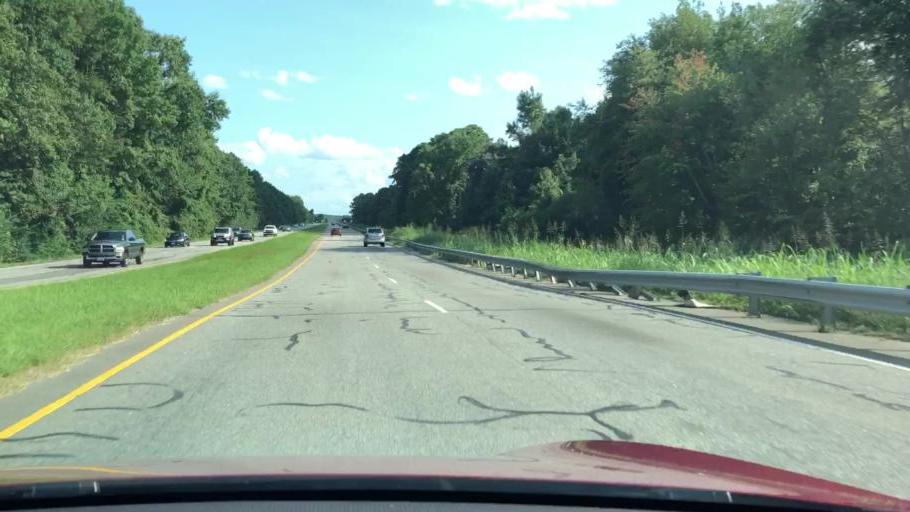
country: US
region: Virginia
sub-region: City of Virginia Beach
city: Virginia Beach
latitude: 36.8353
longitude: -76.0127
